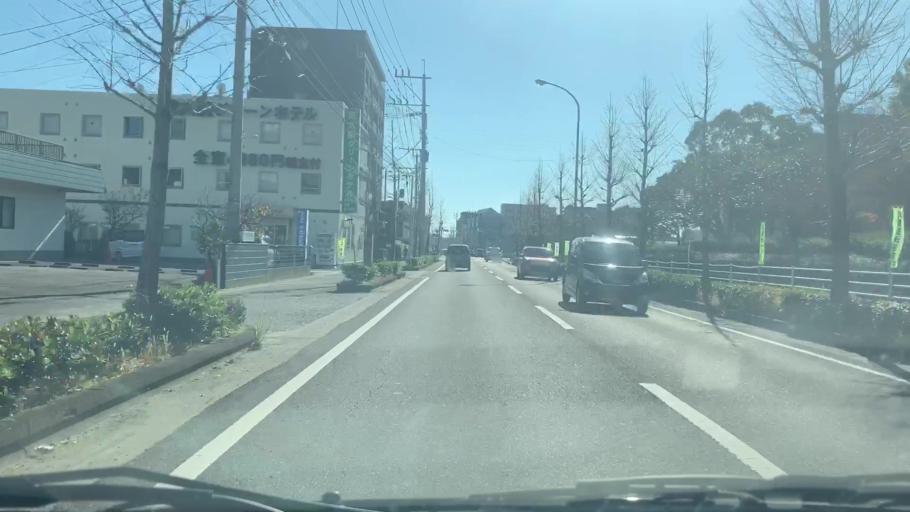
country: JP
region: Saga Prefecture
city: Saga-shi
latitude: 33.2848
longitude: 130.2685
